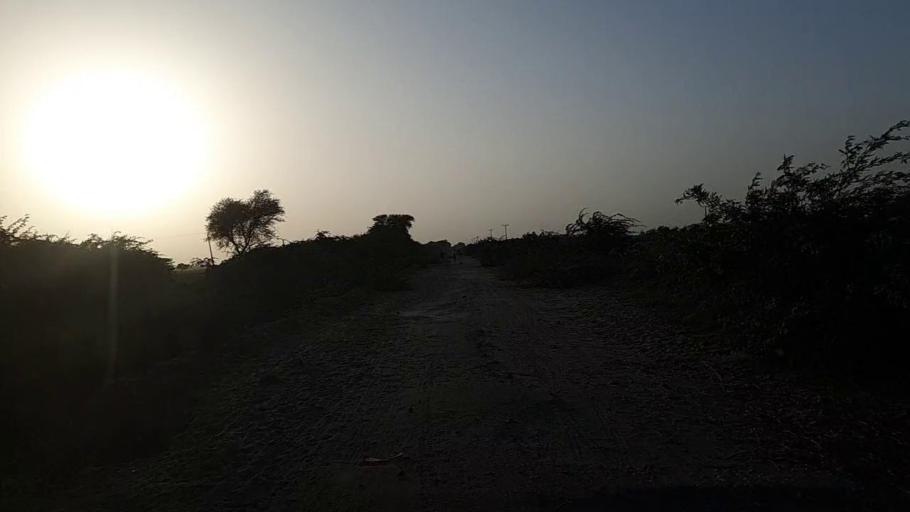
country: PK
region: Sindh
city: Kario
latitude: 24.7083
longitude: 68.4641
